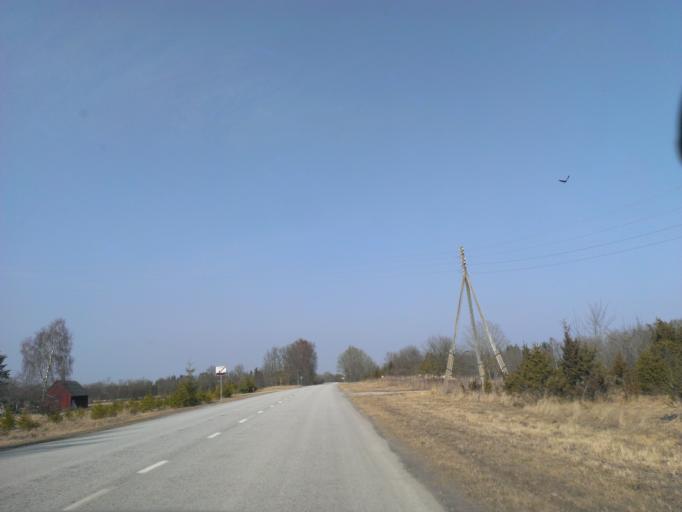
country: EE
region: Saare
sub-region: Orissaare vald
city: Orissaare
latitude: 58.5071
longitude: 23.1128
